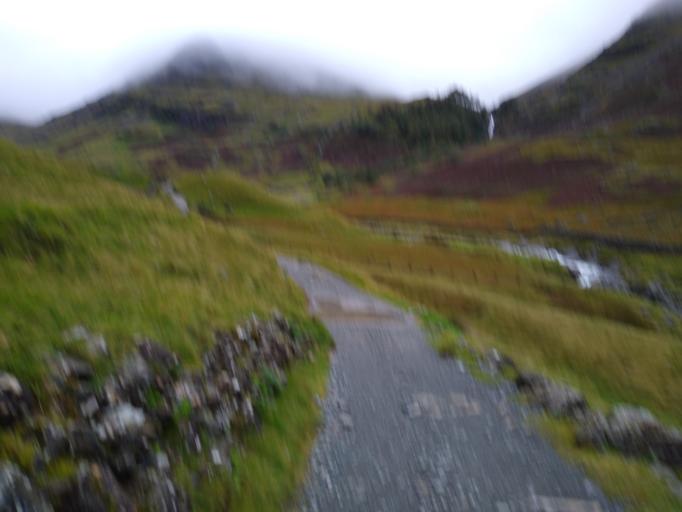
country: GB
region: England
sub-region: Cumbria
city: Keswick
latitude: 54.4920
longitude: -3.1825
